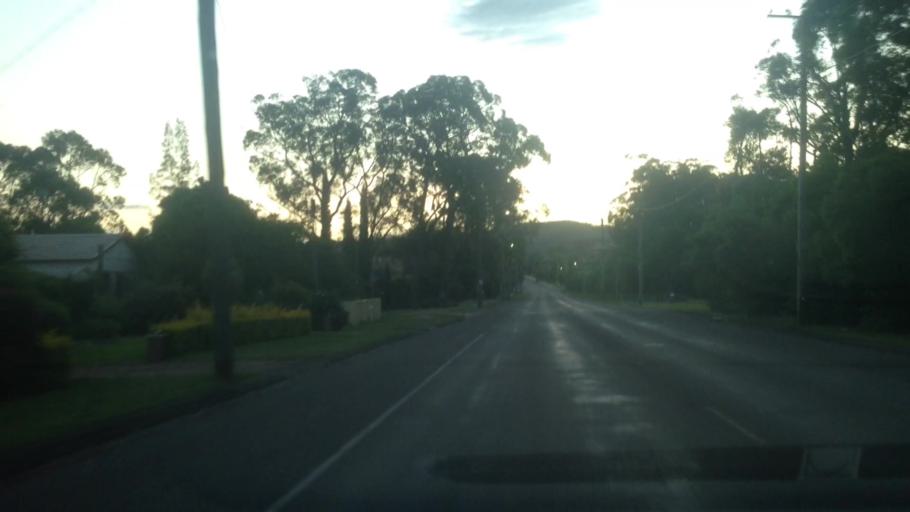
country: AU
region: New South Wales
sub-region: Lake Macquarie Shire
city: Cooranbong
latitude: -33.0718
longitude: 151.4611
